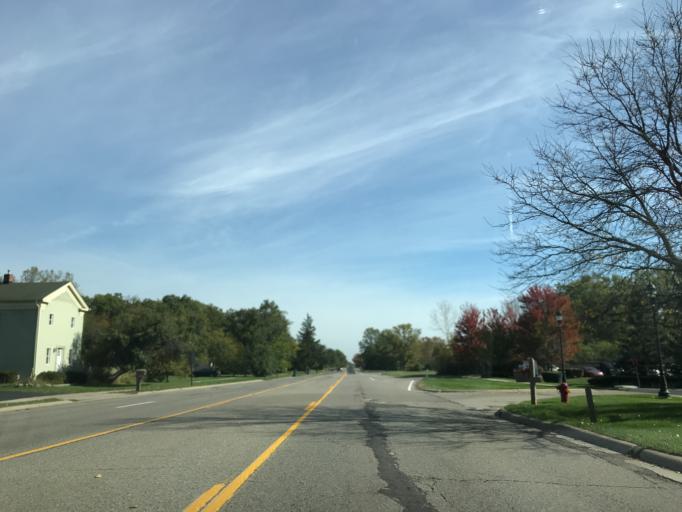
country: US
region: Michigan
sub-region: Oakland County
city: Farmington
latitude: 42.4703
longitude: -83.3526
